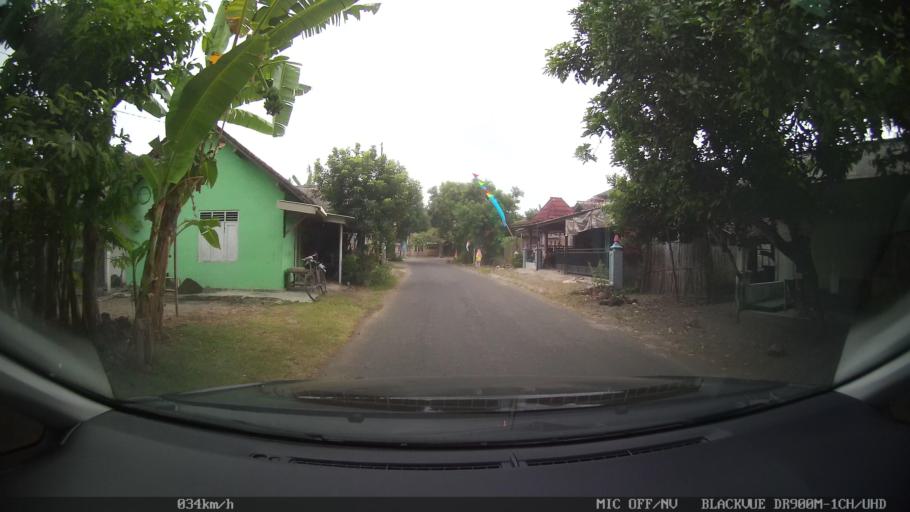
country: ID
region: Daerah Istimewa Yogyakarta
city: Sewon
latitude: -7.8710
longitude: 110.4168
